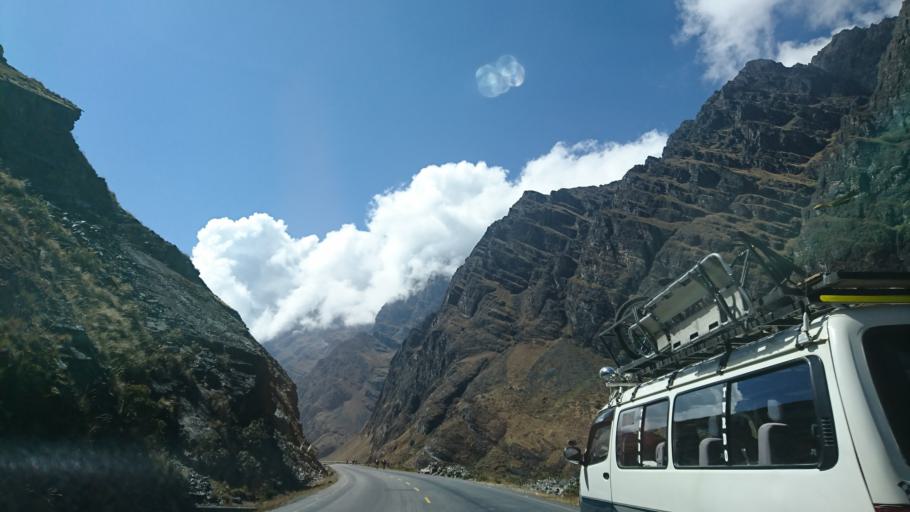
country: BO
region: La Paz
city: La Paz
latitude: -16.3324
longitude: -67.9771
